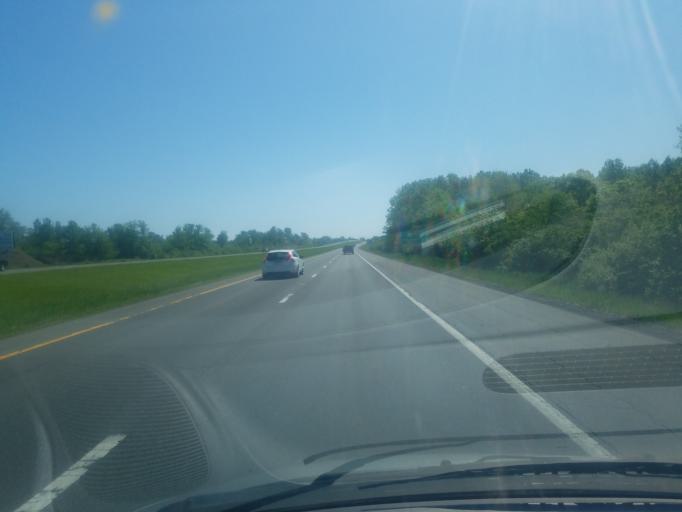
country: US
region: Ohio
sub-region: Erie County
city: Huron
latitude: 41.4052
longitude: -82.6141
